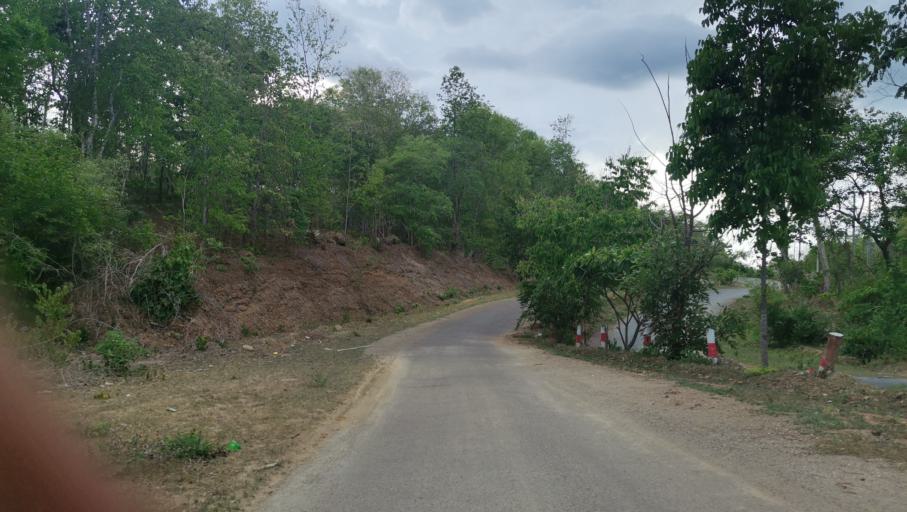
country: MM
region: Magway
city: Minbu
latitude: 20.1029
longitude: 94.5493
